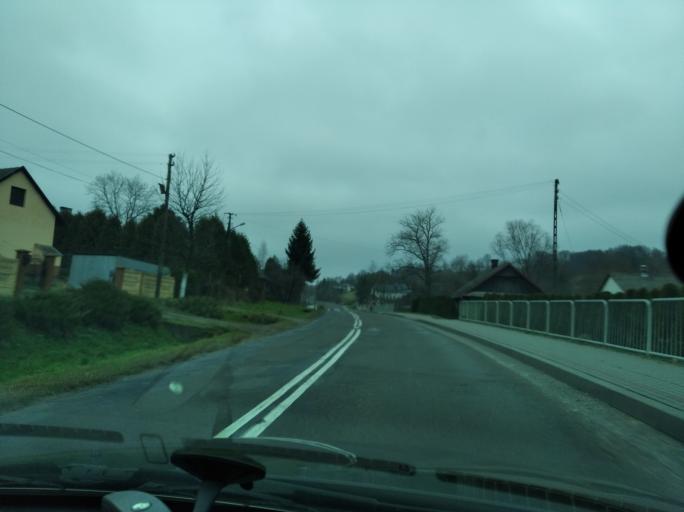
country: PL
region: Subcarpathian Voivodeship
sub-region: Powiat przeworski
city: Jawornik Polski
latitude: 49.8779
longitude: 22.2450
